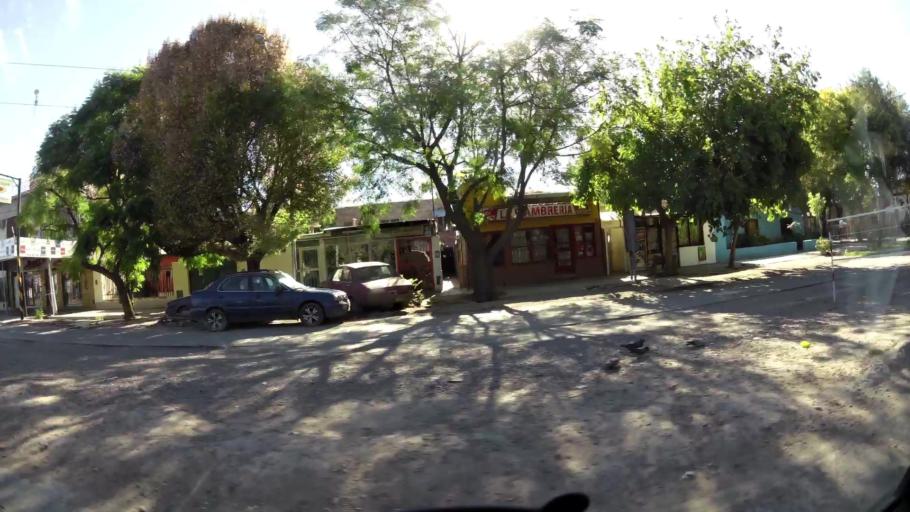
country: AR
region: Mendoza
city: Las Heras
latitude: -32.8606
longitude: -68.8216
